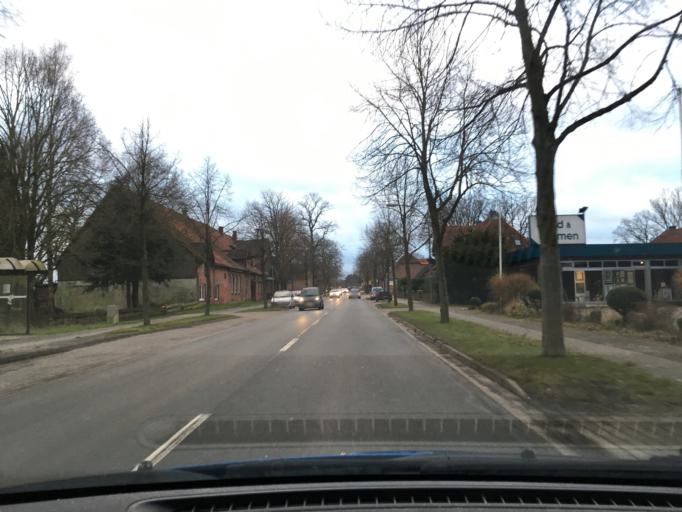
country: DE
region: Lower Saxony
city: Wrestedt
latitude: 52.9215
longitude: 10.5259
